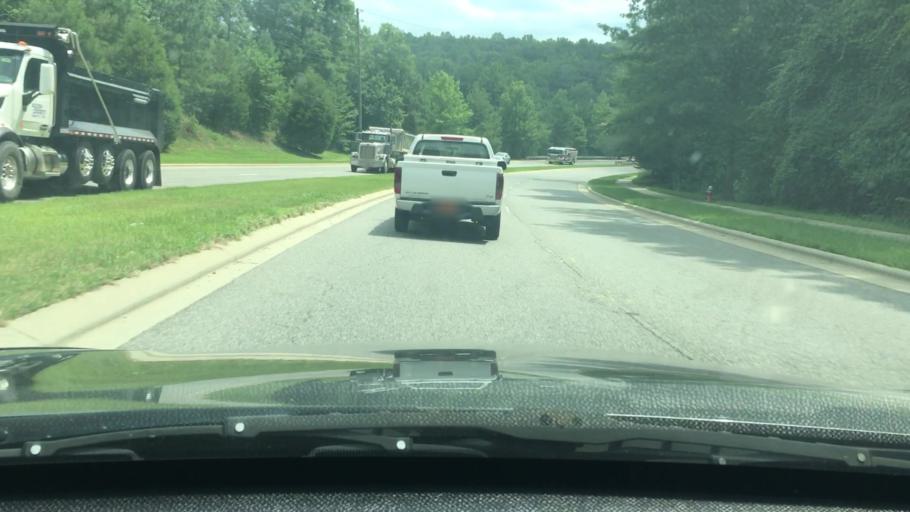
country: US
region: North Carolina
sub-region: Wake County
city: West Raleigh
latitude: 35.8466
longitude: -78.7106
